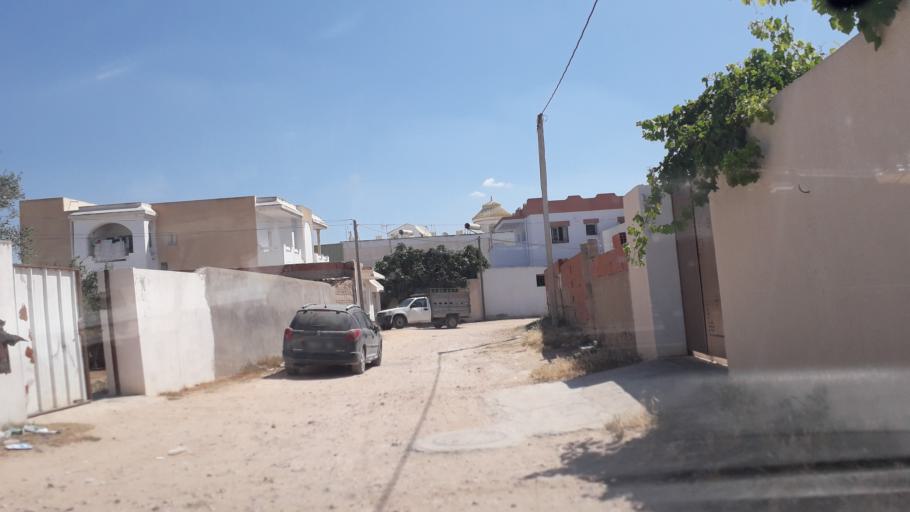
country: TN
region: Safaqis
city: Al Qarmadah
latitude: 34.8177
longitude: 10.7653
